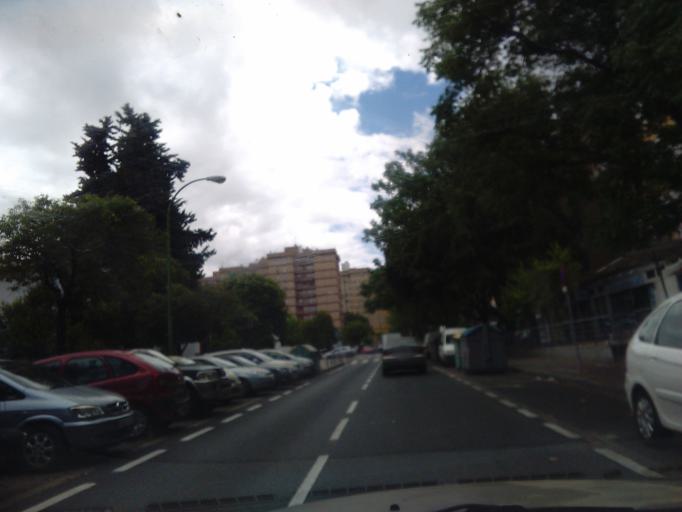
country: ES
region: Andalusia
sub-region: Provincia de Sevilla
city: Sevilla
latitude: 37.3752
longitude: -5.9529
